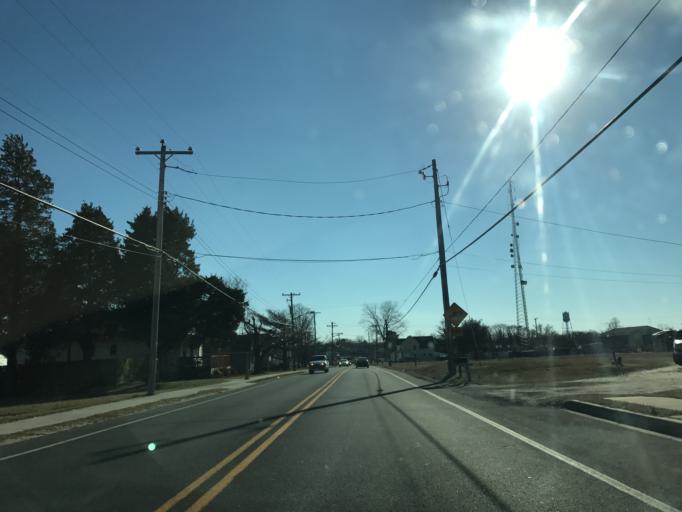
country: US
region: Maryland
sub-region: Caroline County
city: Denton
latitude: 38.8911
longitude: -75.8223
